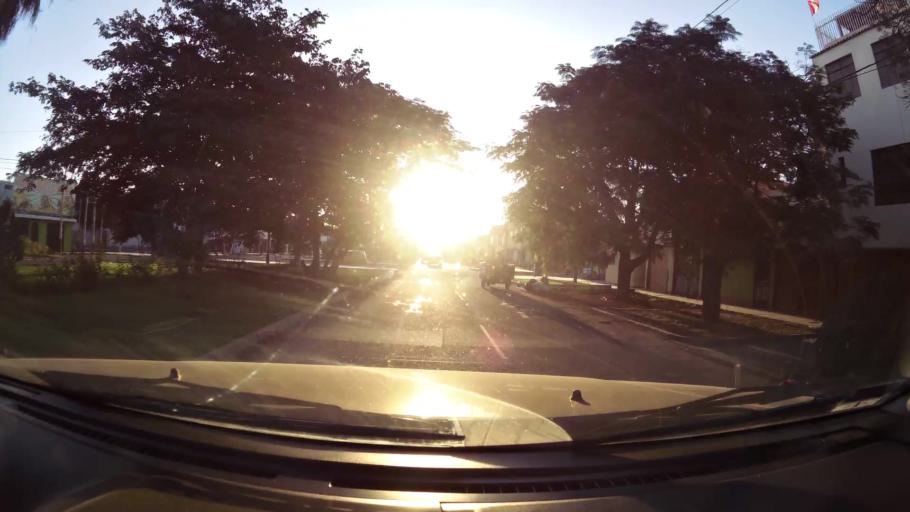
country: PE
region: Ica
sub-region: Provincia de Ica
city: Ica
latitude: -14.0848
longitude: -75.7247
